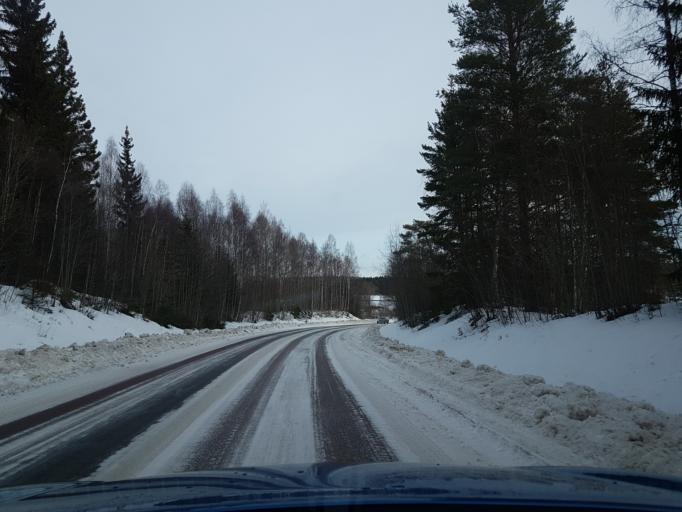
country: SE
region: Dalarna
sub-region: Leksand Municipality
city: Leksand
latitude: 60.7559
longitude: 15.0165
